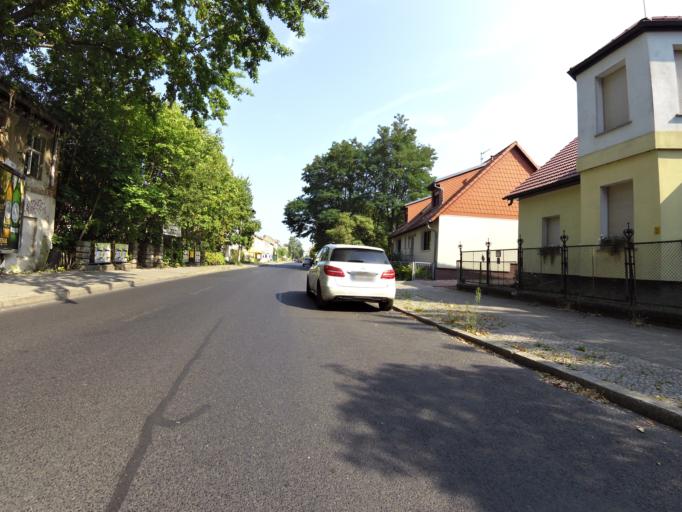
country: DE
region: Berlin
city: Altglienicke
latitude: 52.4193
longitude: 13.5429
